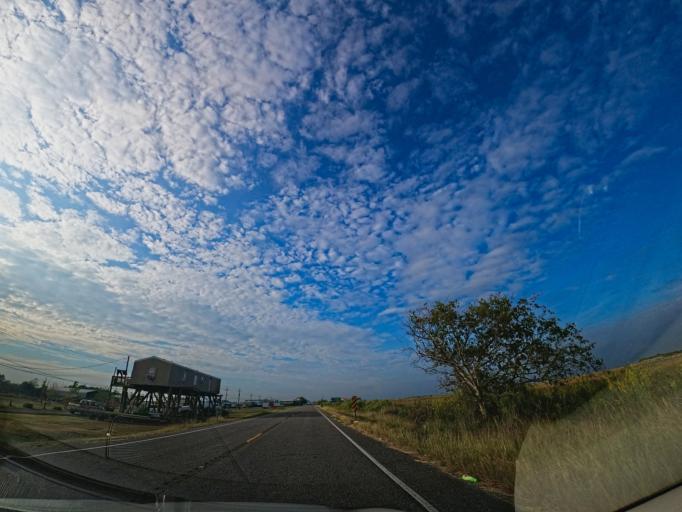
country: US
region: Louisiana
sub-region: Terrebonne Parish
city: Dulac
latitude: 29.3271
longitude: -90.6442
